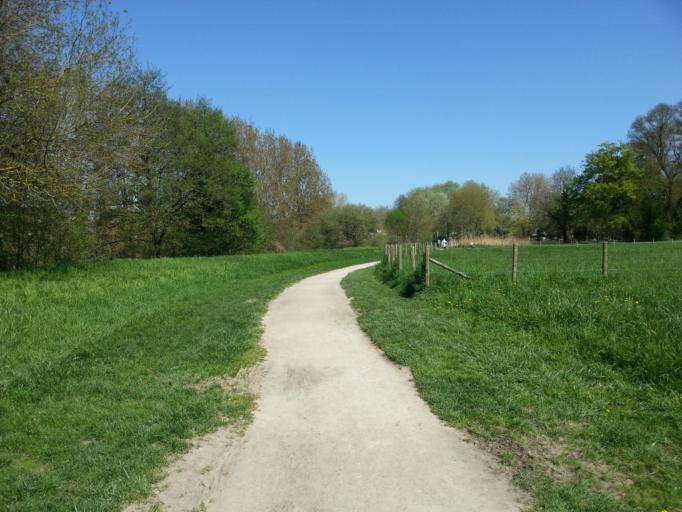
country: FR
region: Pays de la Loire
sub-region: Departement de la Sarthe
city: Le Mans
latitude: 47.9916
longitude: 0.1851
